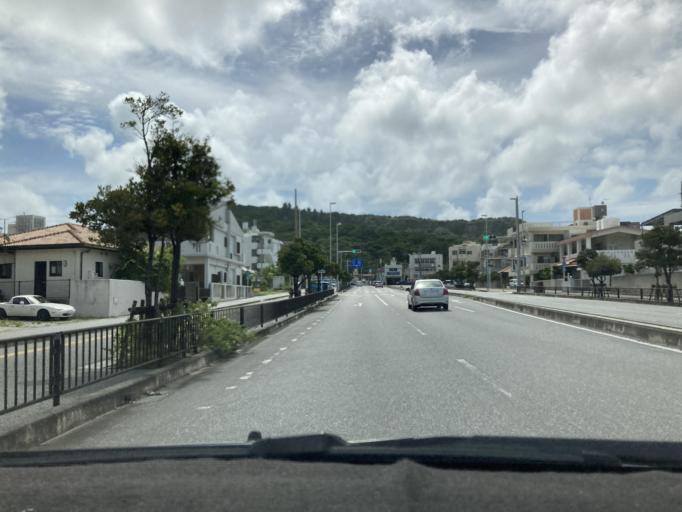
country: JP
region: Okinawa
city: Ginowan
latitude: 26.2018
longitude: 127.7605
